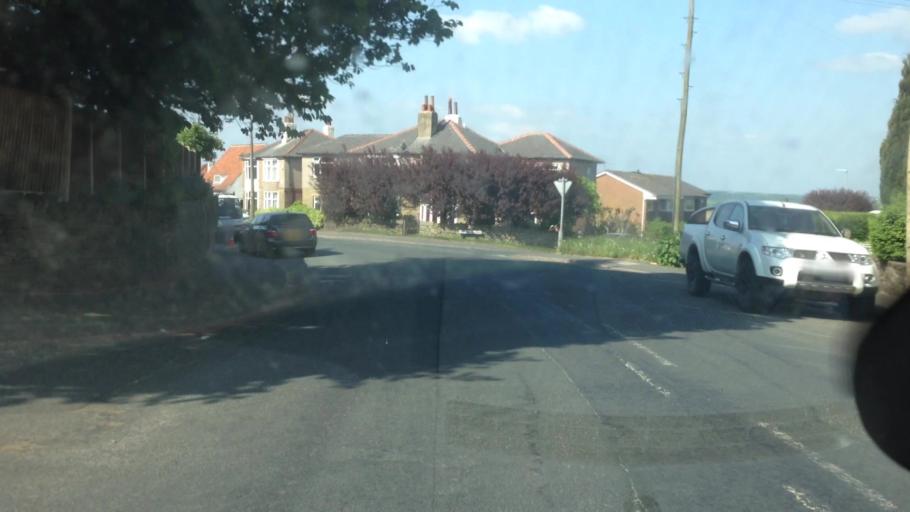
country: GB
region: England
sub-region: Calderdale
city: Brighouse
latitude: 53.6833
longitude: -1.7966
